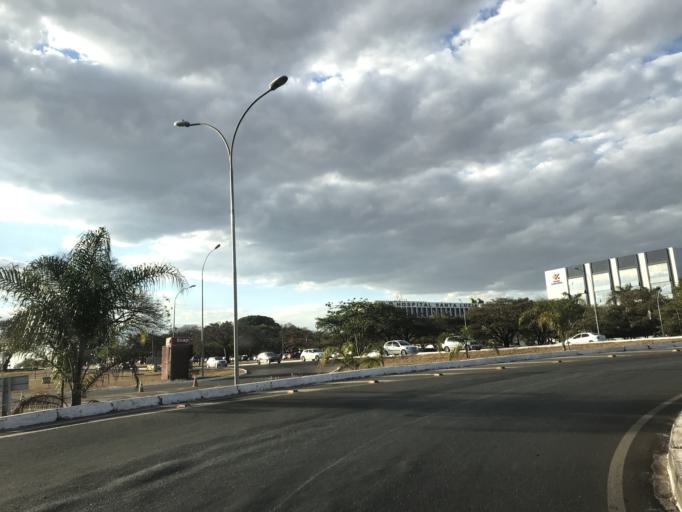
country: BR
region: Federal District
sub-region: Brasilia
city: Brasilia
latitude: -15.8297
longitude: -47.9306
